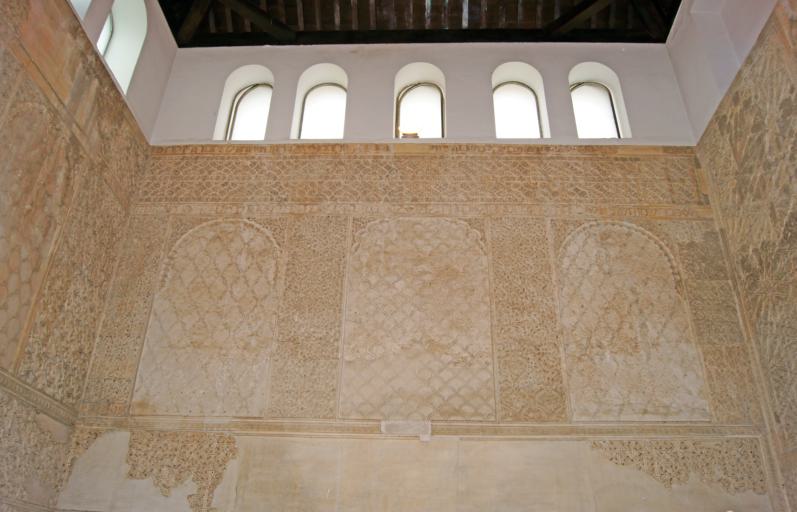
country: ES
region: Andalusia
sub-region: Province of Cordoba
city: Cordoba
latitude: 37.8798
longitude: -4.7834
